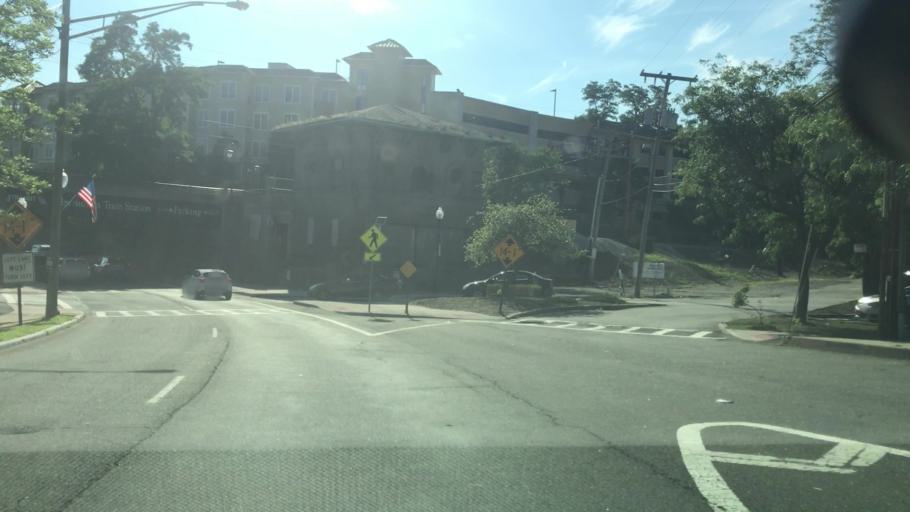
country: US
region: New Jersey
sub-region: Morris County
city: Morristown
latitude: 40.7981
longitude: -74.4738
